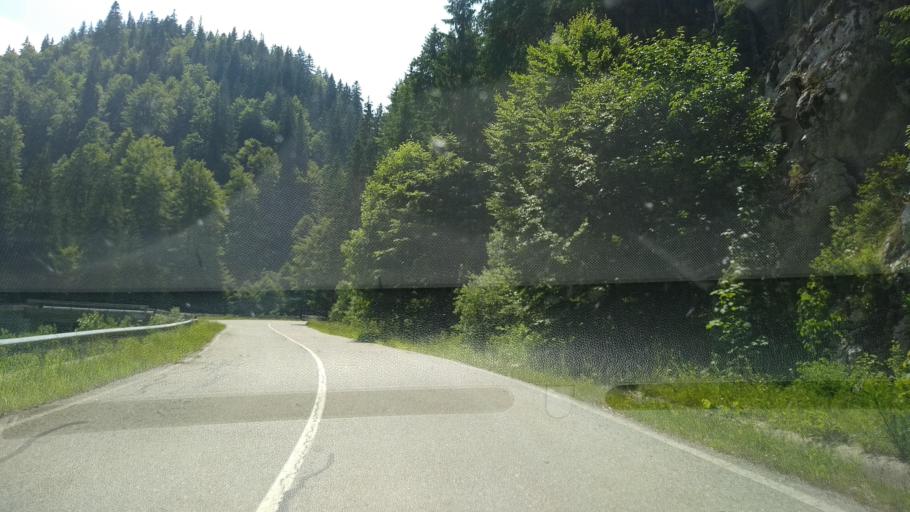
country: RO
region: Hunedoara
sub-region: Comuna Rau de Mori
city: Rau de Mori
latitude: 45.2777
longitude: 22.9100
